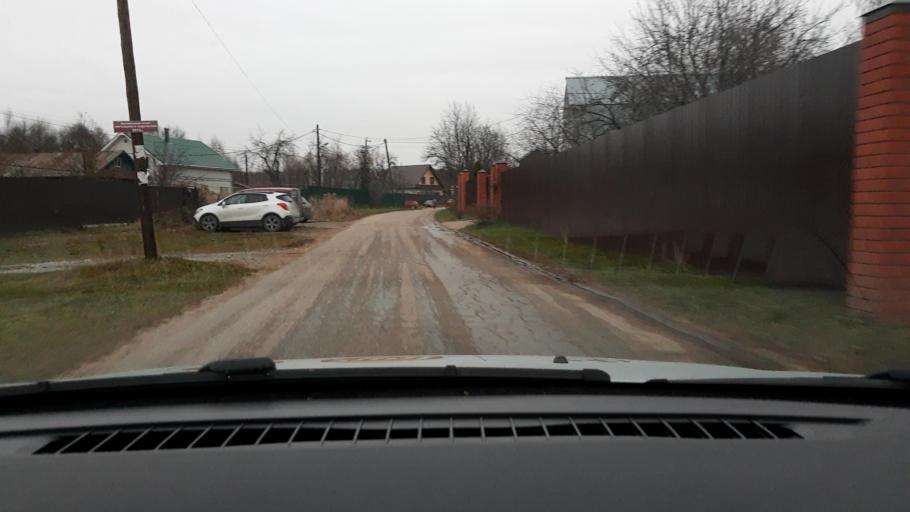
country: RU
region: Nizjnij Novgorod
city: Neklyudovo
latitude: 56.4183
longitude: 44.0209
